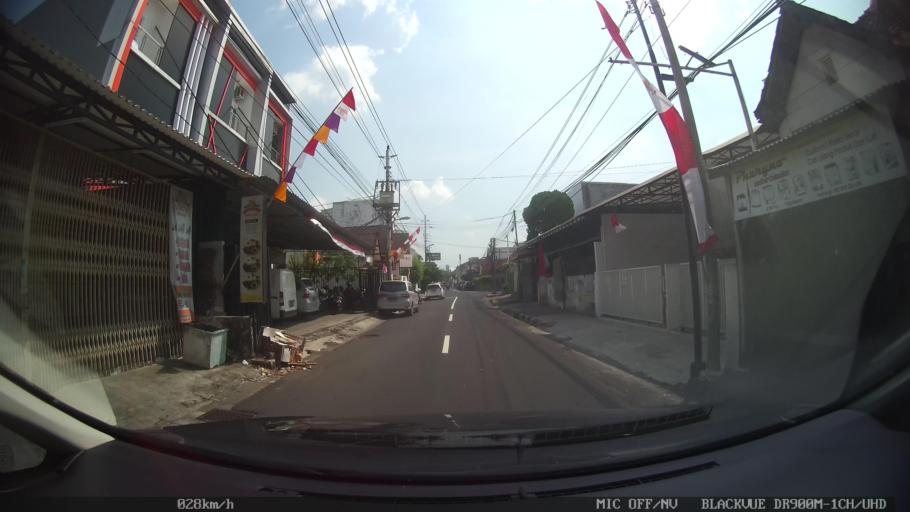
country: ID
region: Daerah Istimewa Yogyakarta
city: Yogyakarta
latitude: -7.7858
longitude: 110.3629
